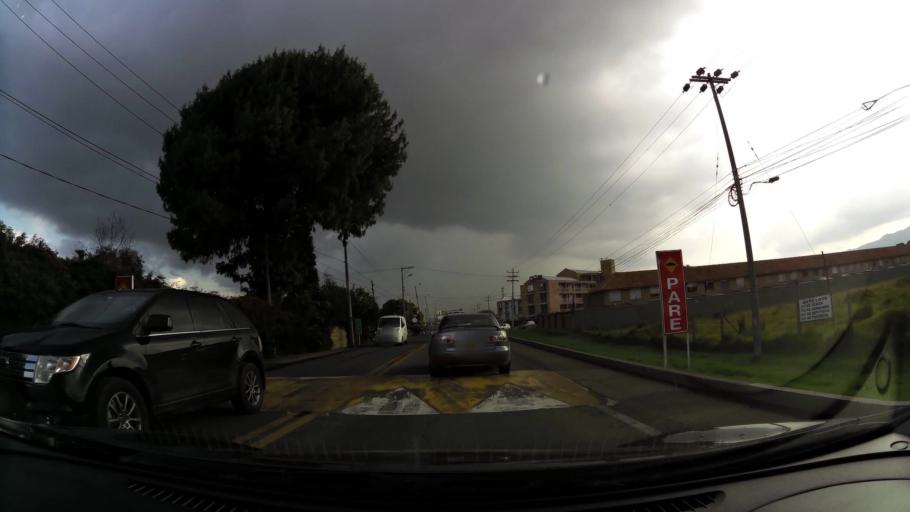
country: CO
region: Cundinamarca
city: Chia
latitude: 4.8576
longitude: -74.0482
